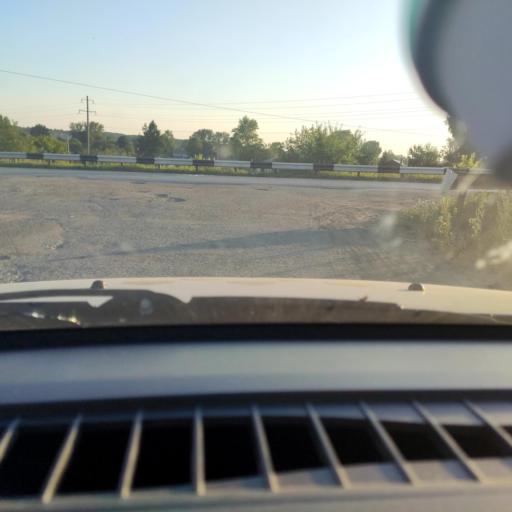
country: RU
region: Perm
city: Kungur
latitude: 57.4385
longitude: 57.0150
